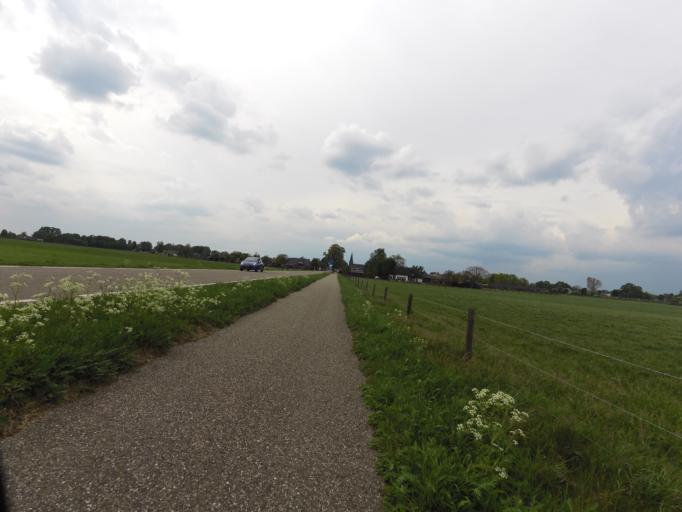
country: NL
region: Gelderland
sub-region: Gemeente Montferland
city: s-Heerenberg
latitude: 51.9330
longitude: 6.2376
